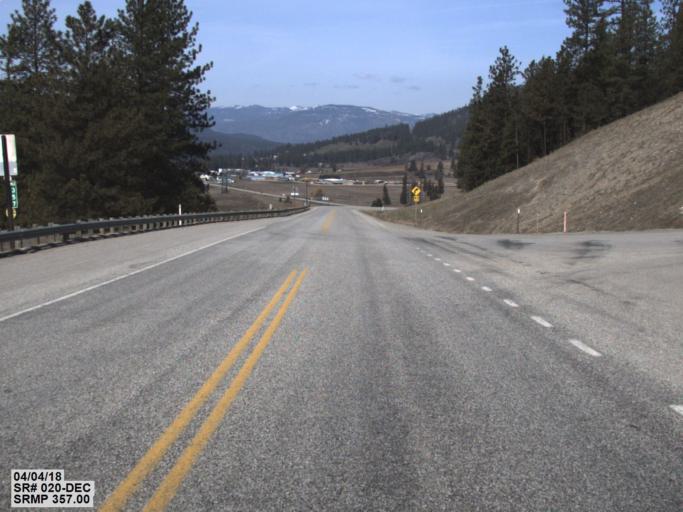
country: US
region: Washington
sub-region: Stevens County
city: Colville
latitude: 48.5436
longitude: -117.8506
